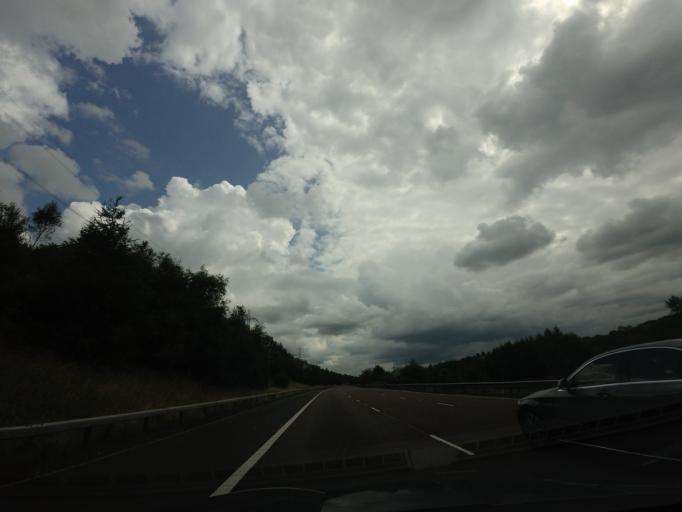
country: GB
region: Scotland
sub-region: Dumfries and Galloway
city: Moffat
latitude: 55.3258
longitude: -3.4705
